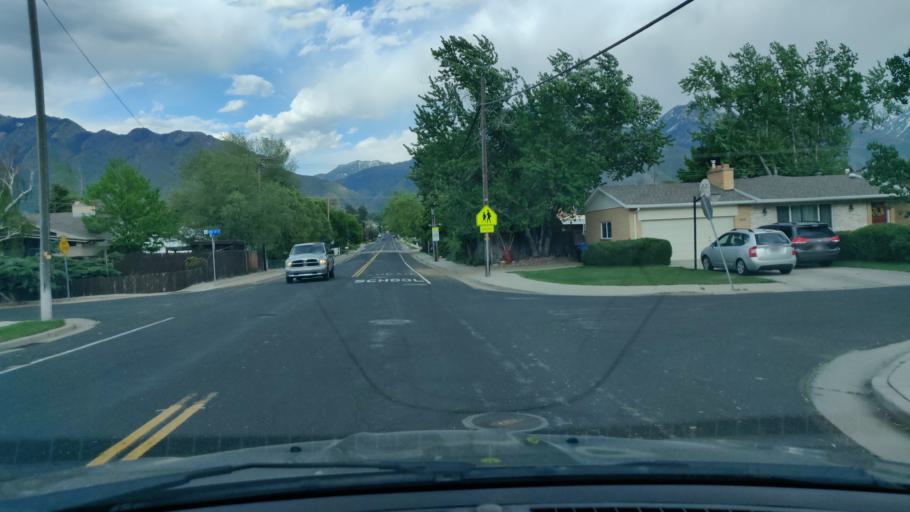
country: US
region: Utah
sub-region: Salt Lake County
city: Little Cottonwood Creek Valley
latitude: 40.6204
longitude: -111.8423
